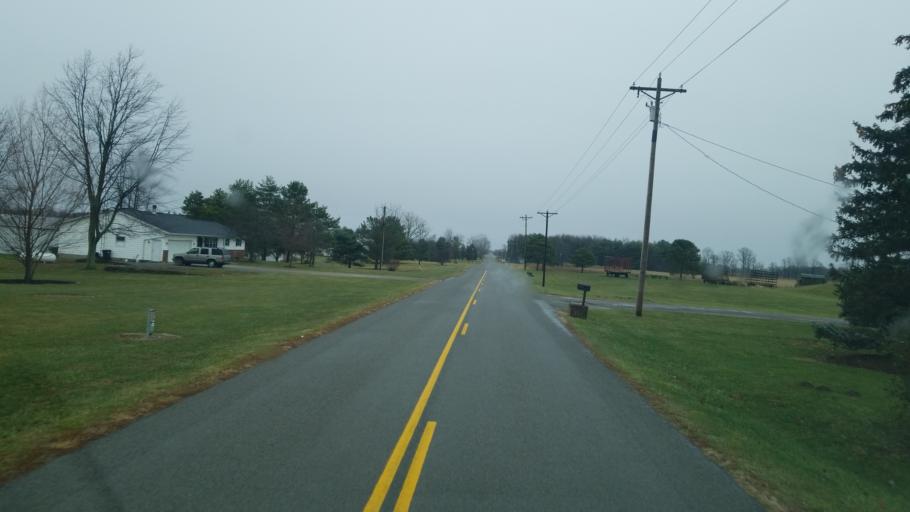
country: US
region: Ohio
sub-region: Logan County
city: Northwood
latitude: 40.4474
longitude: -83.6190
